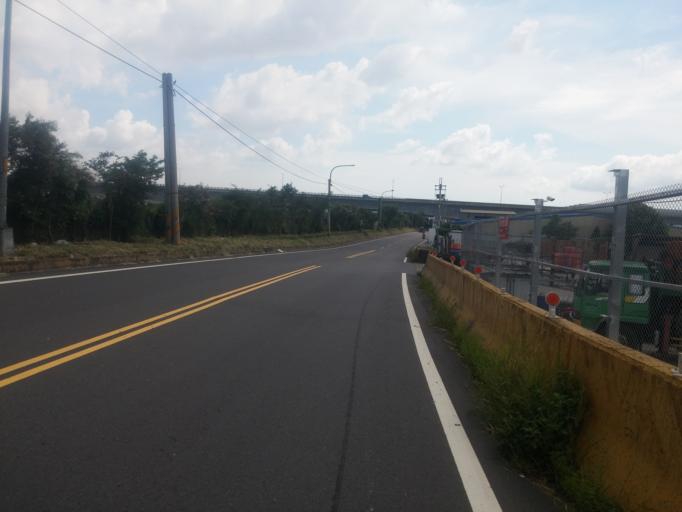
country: TW
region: Taiwan
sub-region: Taichung City
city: Taichung
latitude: 24.0736
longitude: 120.6911
